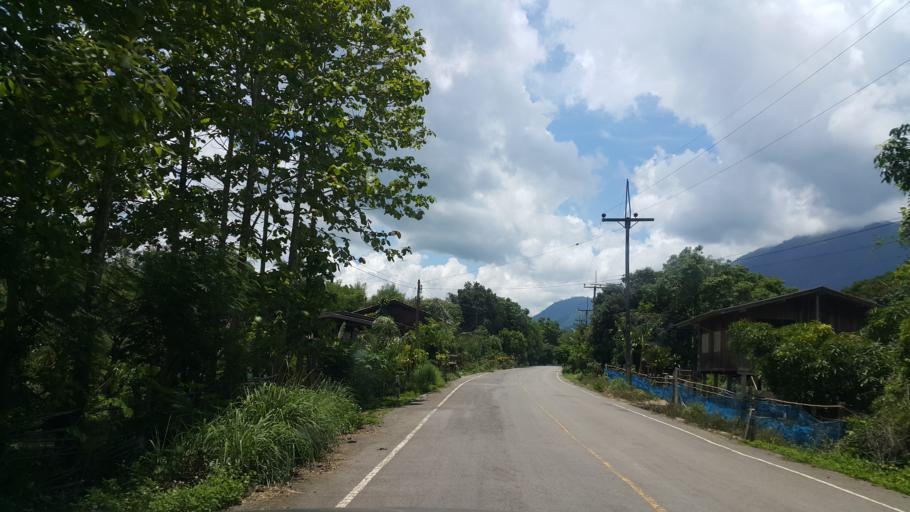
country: TH
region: Phayao
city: Phayao
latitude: 19.1785
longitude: 99.7904
